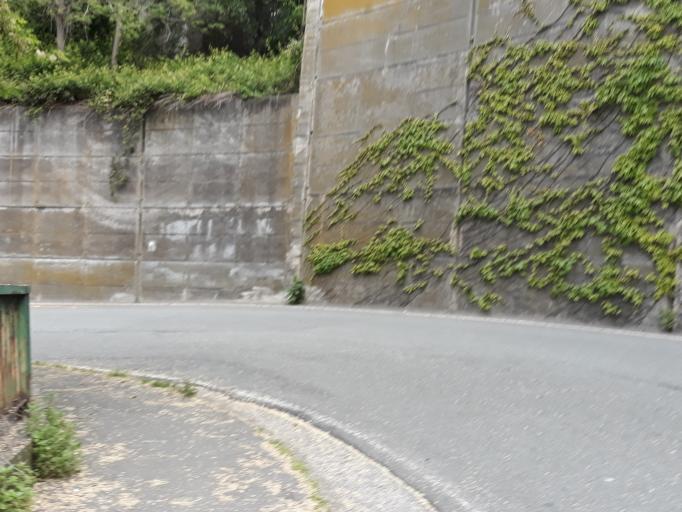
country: IT
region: Liguria
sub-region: Provincia di Genova
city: Mele
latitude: 44.4324
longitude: 8.7699
